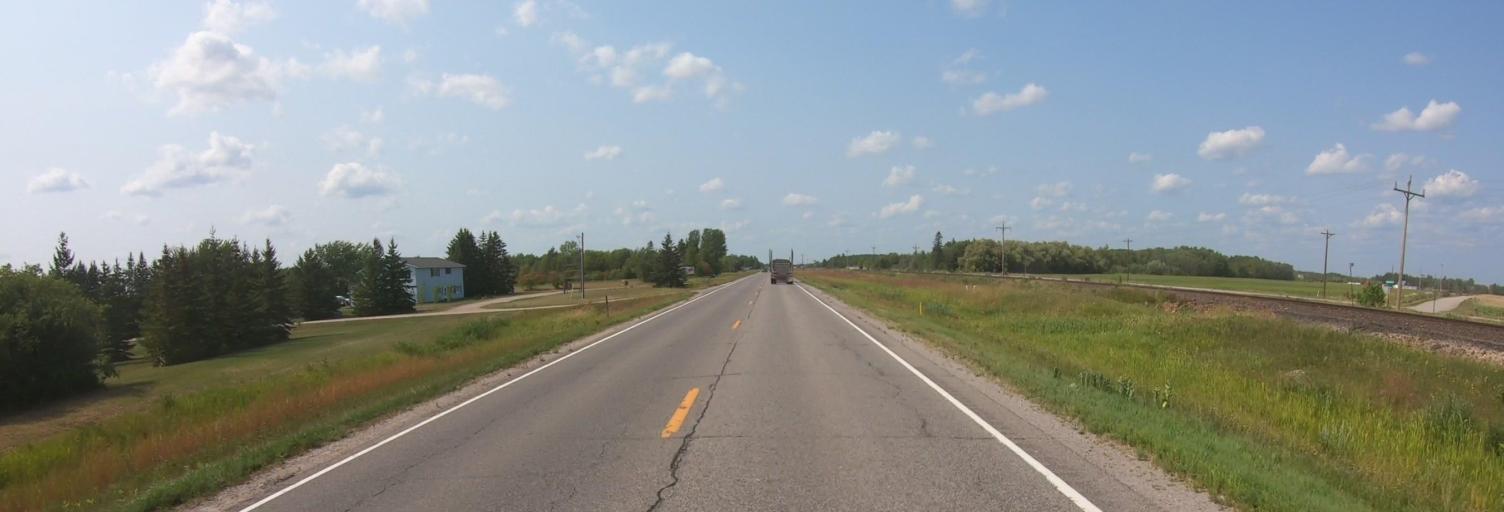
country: US
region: Minnesota
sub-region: Roseau County
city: Warroad
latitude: 48.8837
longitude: -95.2925
